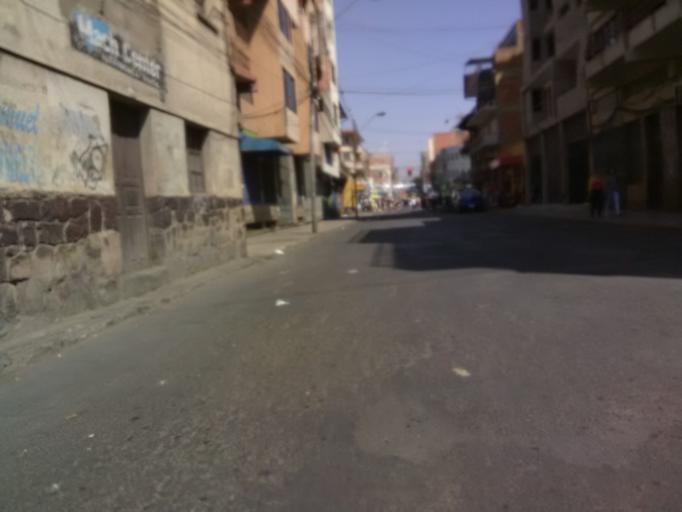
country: BO
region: Cochabamba
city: Cochabamba
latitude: -17.3983
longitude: -66.1544
